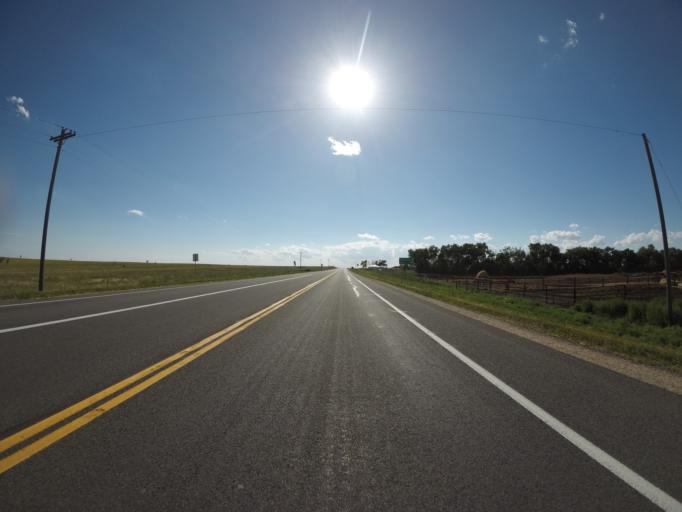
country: US
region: Colorado
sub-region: Morgan County
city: Brush
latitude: 40.6107
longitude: -103.6018
